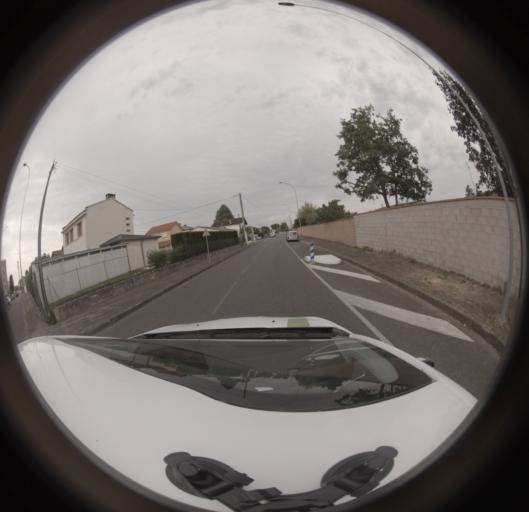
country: FR
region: Midi-Pyrenees
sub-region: Departement du Tarn-et-Garonne
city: Montauban
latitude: 44.0173
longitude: 1.3767
